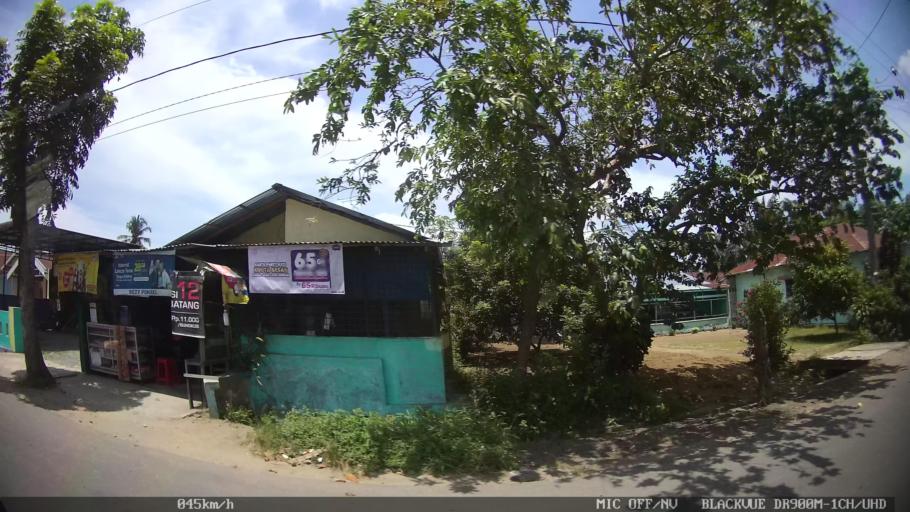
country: ID
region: North Sumatra
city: Binjai
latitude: 3.6001
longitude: 98.5181
